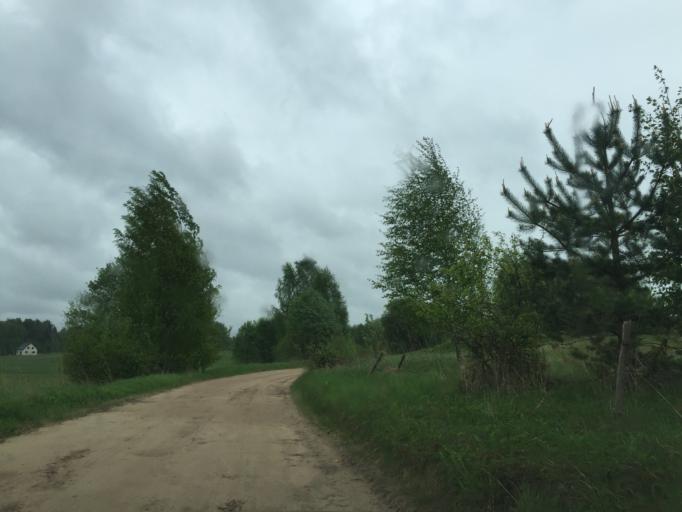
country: LV
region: Kegums
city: Kegums
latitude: 56.7353
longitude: 24.7489
